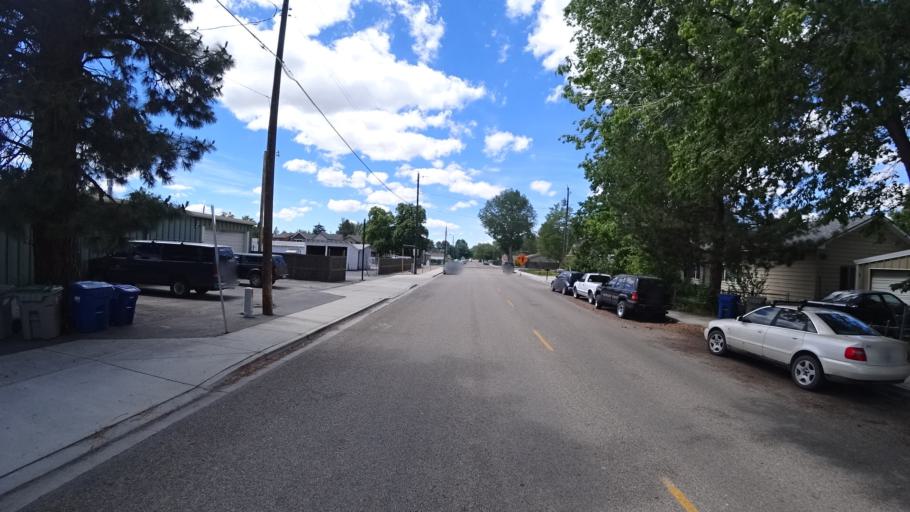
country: US
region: Idaho
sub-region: Ada County
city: Boise
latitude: 43.5946
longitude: -116.1875
